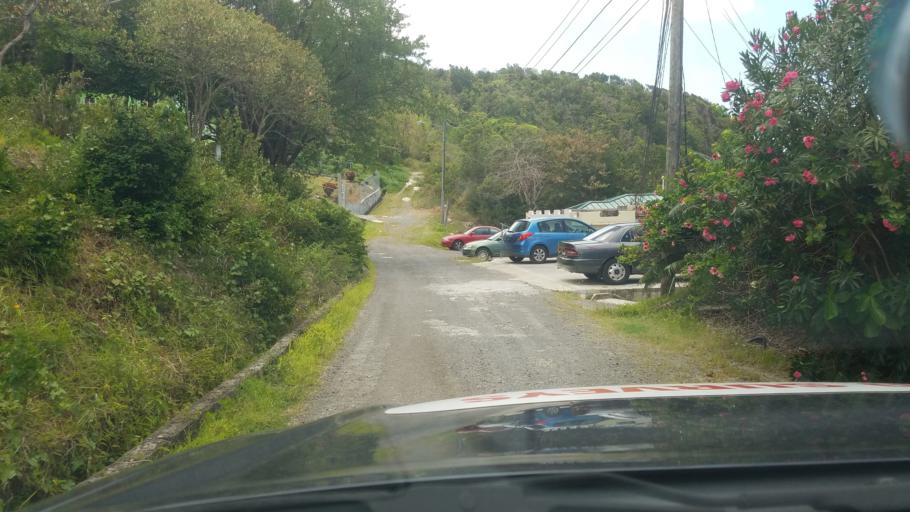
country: LC
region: Castries Quarter
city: Bisee
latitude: 14.0329
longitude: -60.9552
